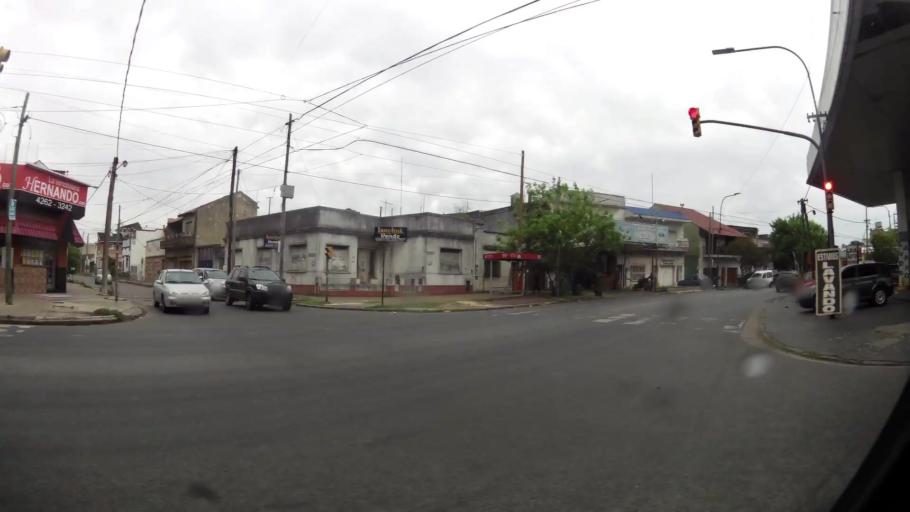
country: AR
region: Buenos Aires
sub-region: Partido de Lanus
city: Lanus
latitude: -34.6879
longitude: -58.4043
